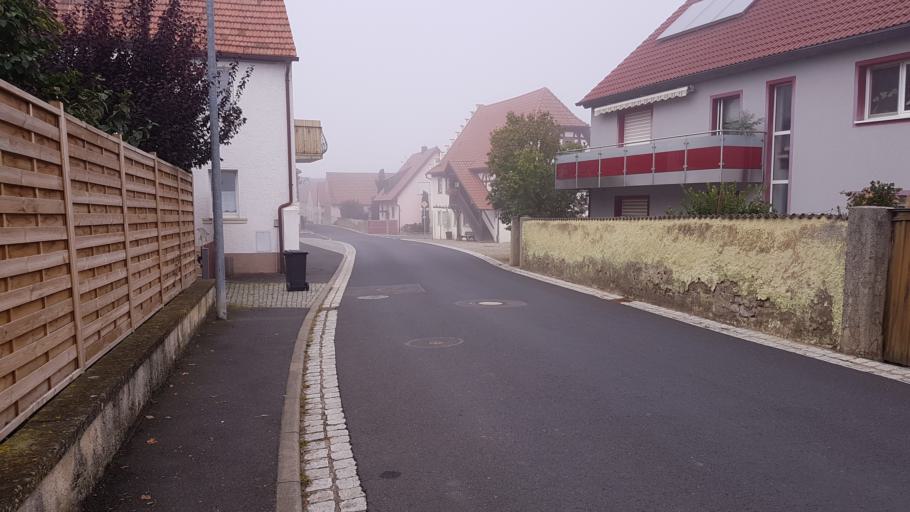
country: DE
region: Bavaria
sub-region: Regierungsbezirk Unterfranken
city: Kolitzheim
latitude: 49.9267
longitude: 10.2032
